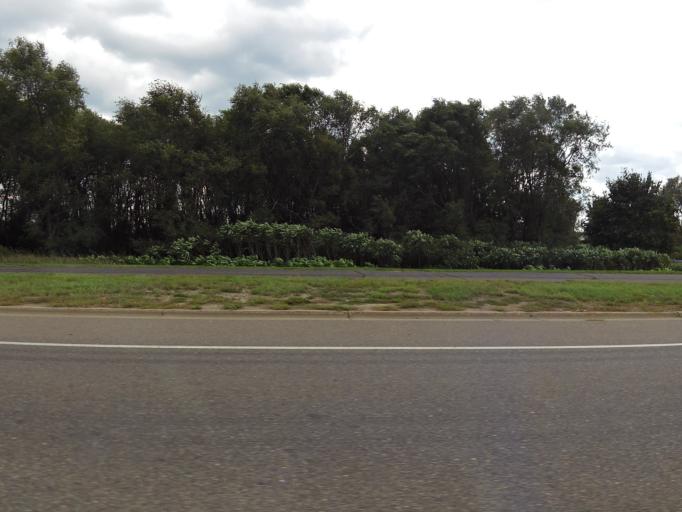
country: US
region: Minnesota
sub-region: Dakota County
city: Apple Valley
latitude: 44.7173
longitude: -93.1805
